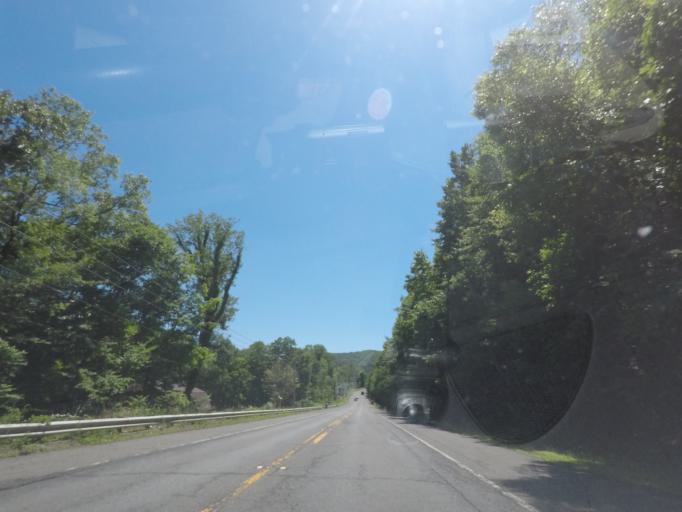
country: US
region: Massachusetts
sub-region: Hampden County
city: Westfield
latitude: 42.1734
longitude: -72.8327
